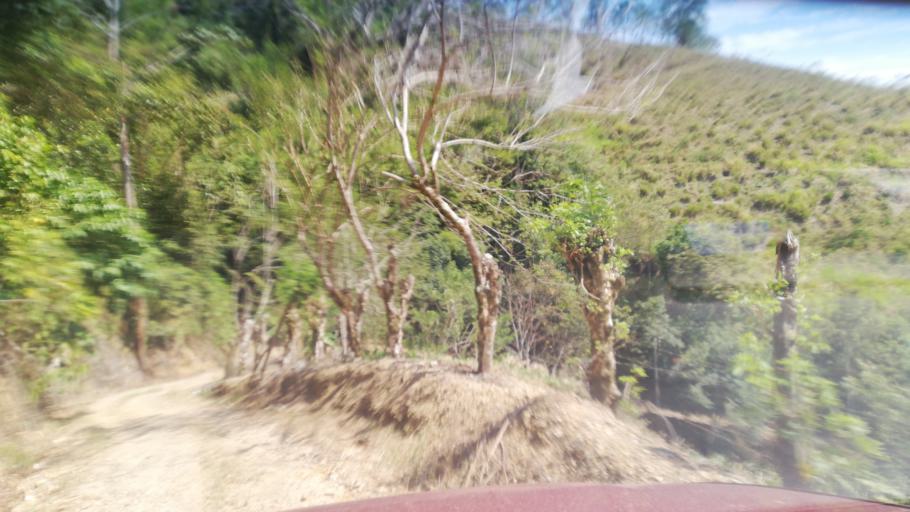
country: CO
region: Risaralda
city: Balboa
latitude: 4.9152
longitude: -75.9514
